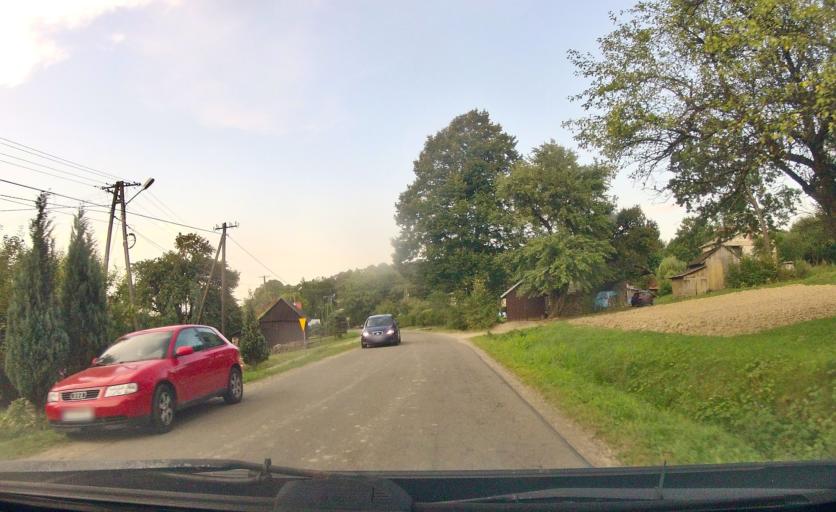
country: PL
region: Subcarpathian Voivodeship
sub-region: Powiat krosnienski
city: Dukla
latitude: 49.5466
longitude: 21.6220
